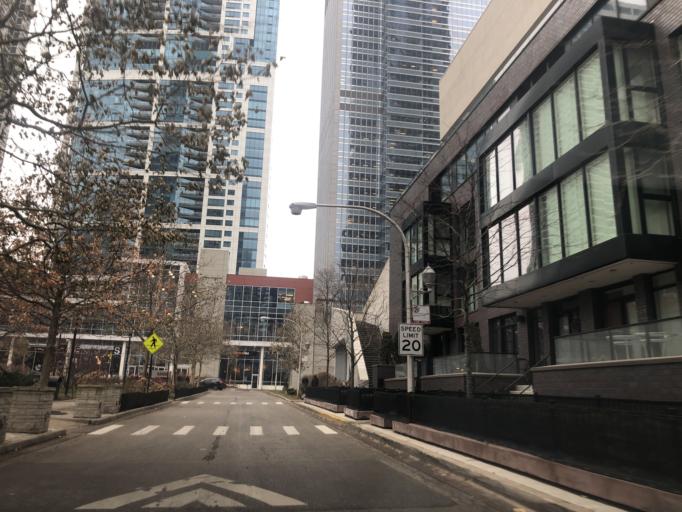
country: US
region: Illinois
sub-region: Cook County
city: Chicago
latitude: 41.8863
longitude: -87.6191
